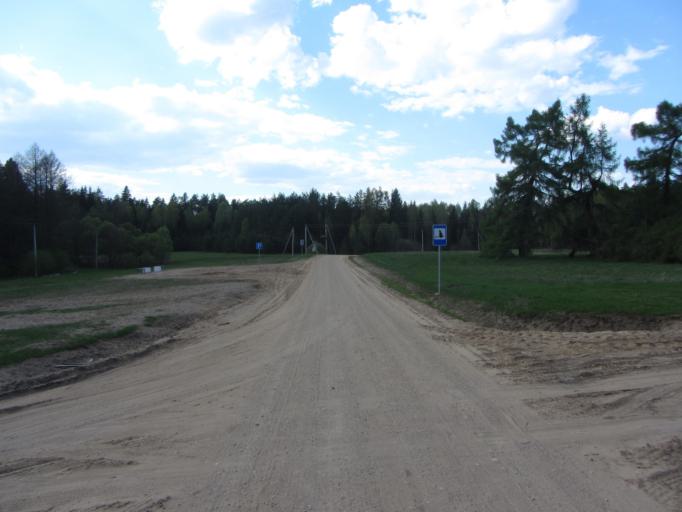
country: LT
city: Svencioneliai
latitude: 55.1672
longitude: 25.8389
